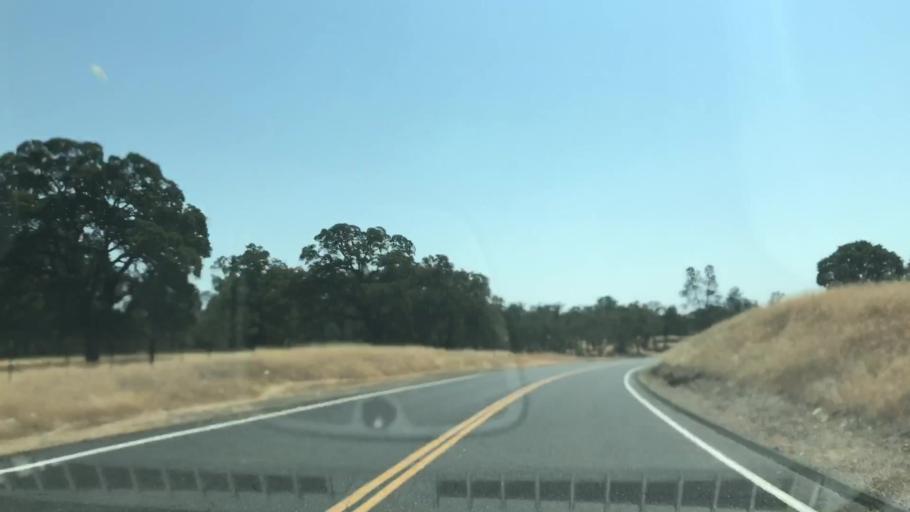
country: US
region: California
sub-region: Calaveras County
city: Copperopolis
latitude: 37.9577
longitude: -120.6133
